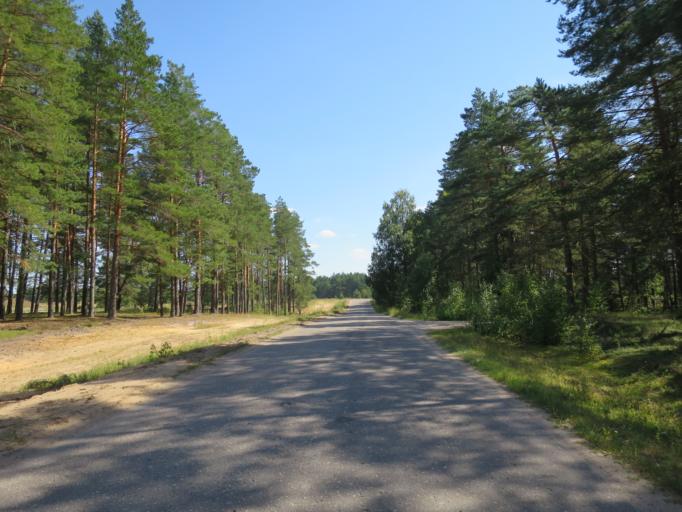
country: LV
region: Garkalne
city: Garkalne
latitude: 57.1028
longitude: 24.3894
